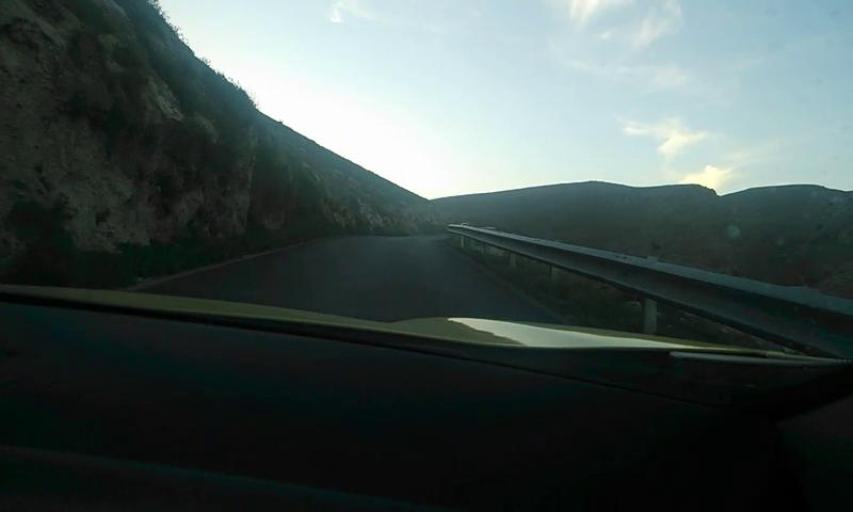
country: PS
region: West Bank
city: Rammun
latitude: 31.9110
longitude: 35.3643
